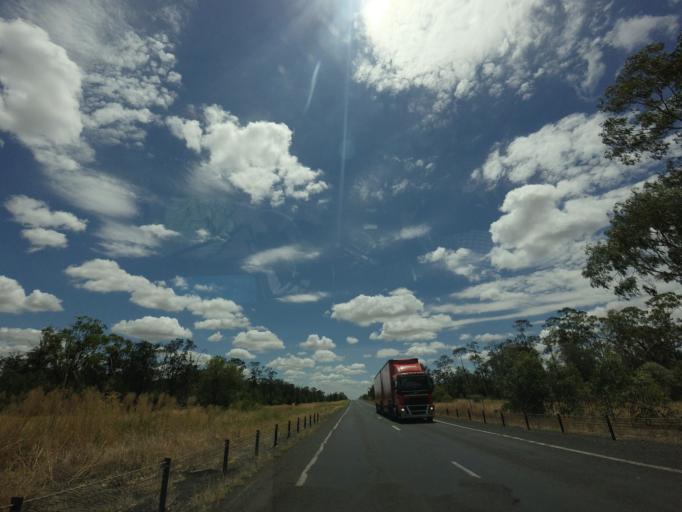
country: AU
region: New South Wales
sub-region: Moree Plains
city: Boggabilla
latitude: -28.8870
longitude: 150.1516
